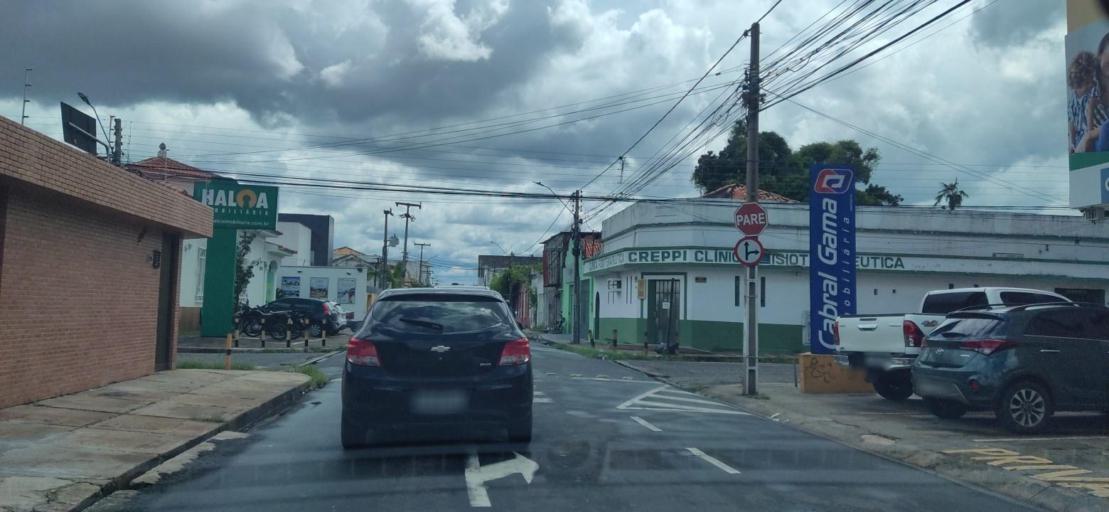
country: BR
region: Piaui
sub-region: Teresina
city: Teresina
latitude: -5.0857
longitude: -42.8112
